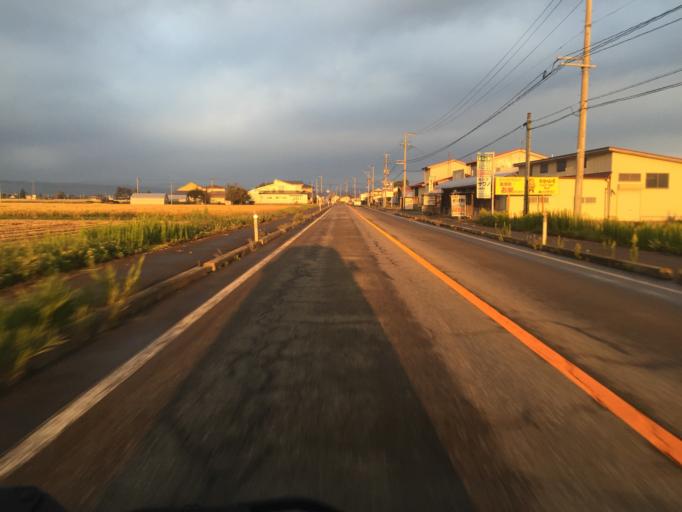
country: JP
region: Fukushima
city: Kitakata
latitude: 37.5536
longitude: 139.8789
